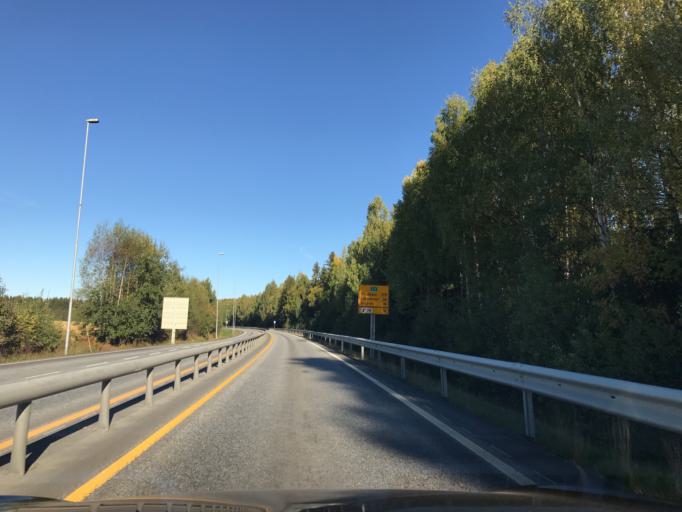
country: NO
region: Hedmark
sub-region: Ringsaker
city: Moelv
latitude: 60.9589
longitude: 10.6229
